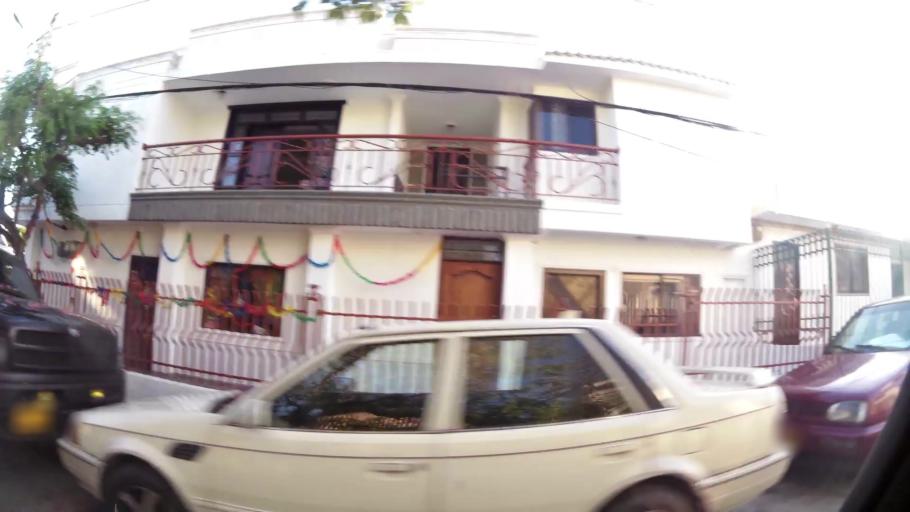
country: CO
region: Atlantico
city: Barranquilla
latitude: 10.9719
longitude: -74.8099
